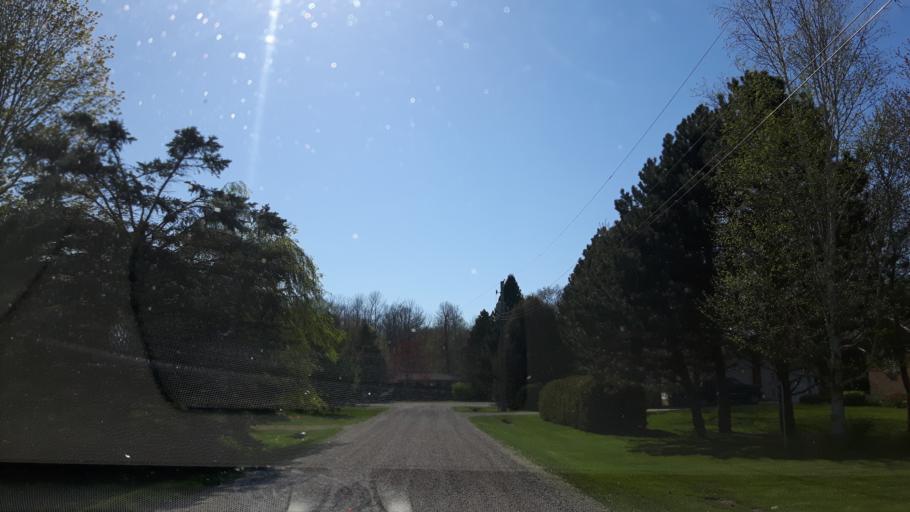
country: CA
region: Ontario
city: Bluewater
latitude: 43.5102
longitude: -81.7078
